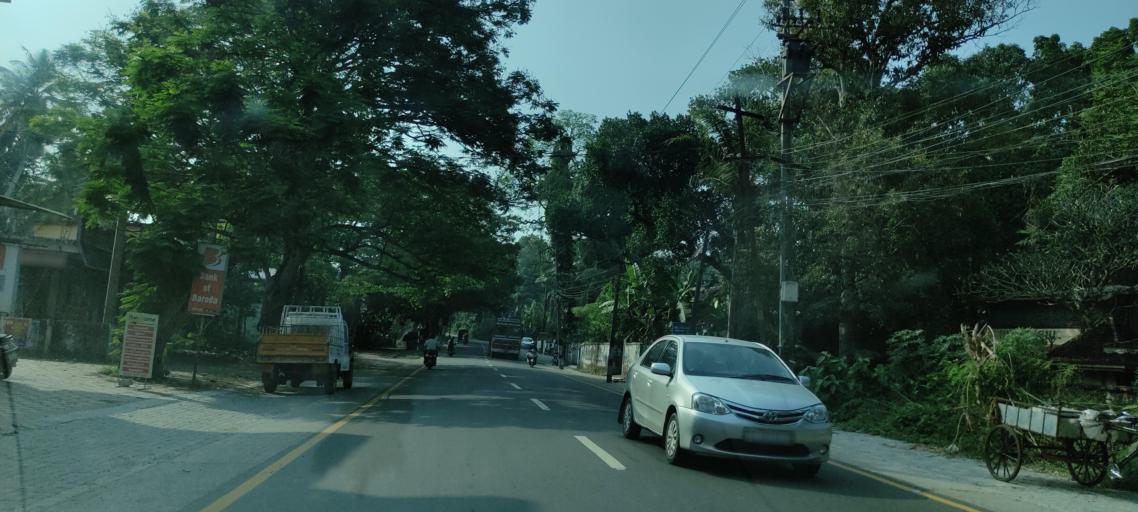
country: IN
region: Kerala
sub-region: Pattanamtitta
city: Tiruvalla
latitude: 9.3691
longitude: 76.5405
